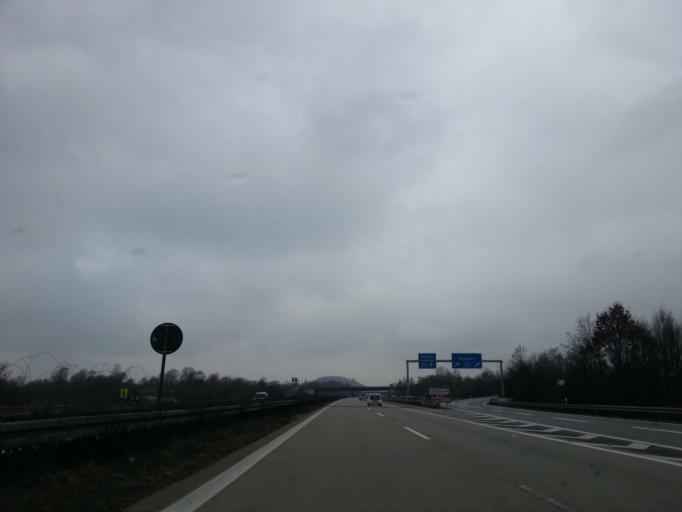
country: DE
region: Bavaria
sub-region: Lower Bavaria
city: Deggendorf
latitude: 48.8169
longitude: 12.9455
